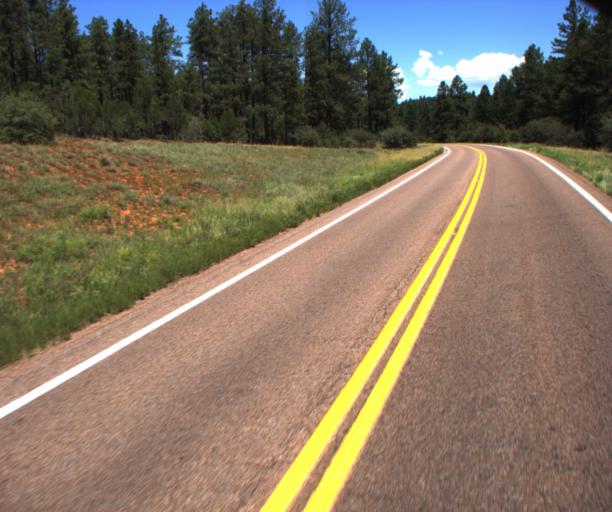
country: US
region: Arizona
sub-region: Navajo County
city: Lake of the Woods
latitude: 34.1301
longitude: -110.1085
